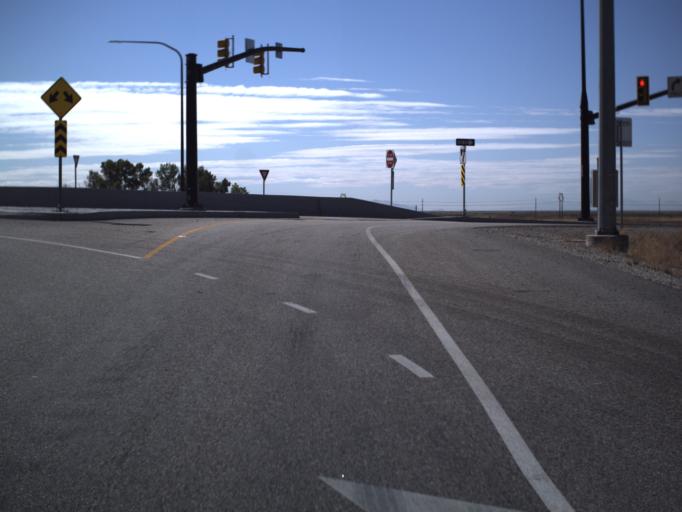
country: US
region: Utah
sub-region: Box Elder County
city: Perry
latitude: 41.4861
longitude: -112.0541
